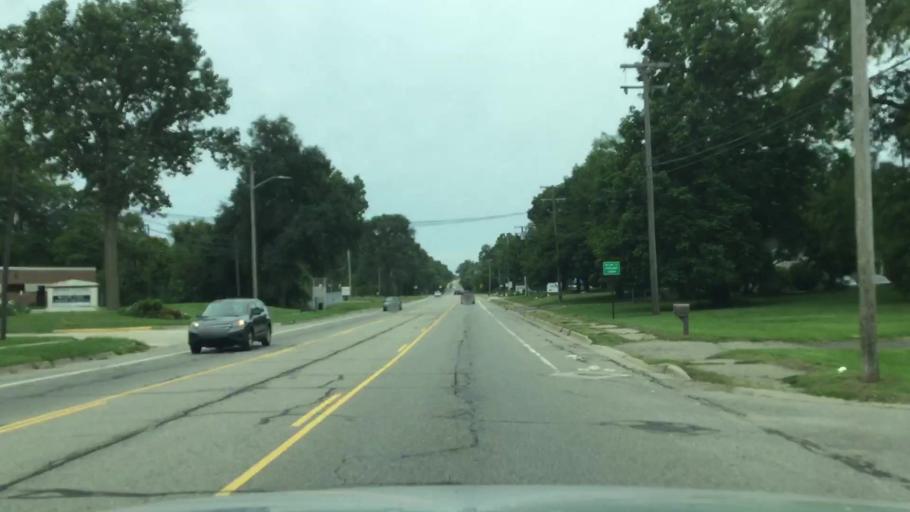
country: US
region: Michigan
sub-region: Washtenaw County
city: Ypsilanti
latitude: 42.2362
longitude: -83.6282
